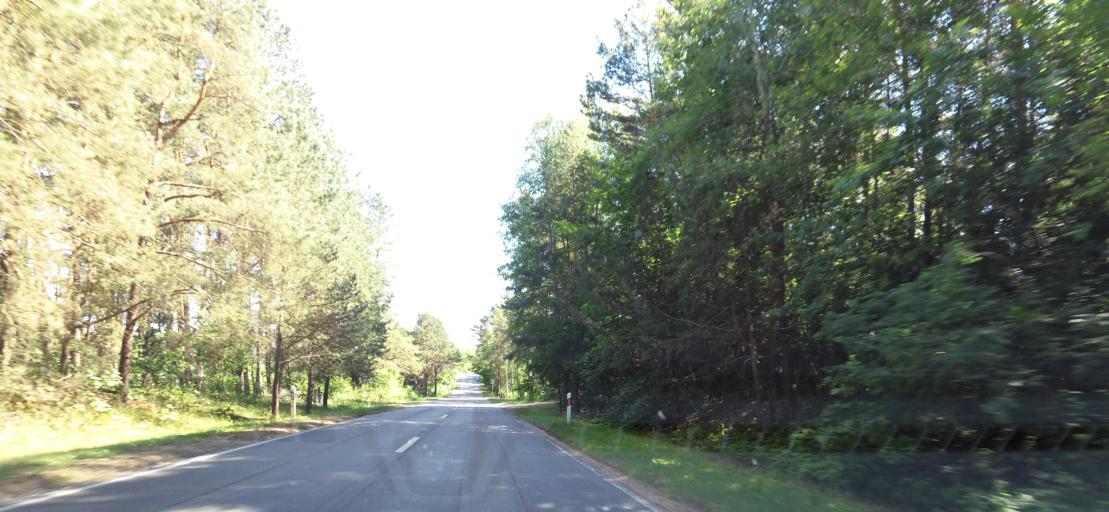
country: LT
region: Vilnius County
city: Rasos
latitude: 54.7941
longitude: 25.3505
